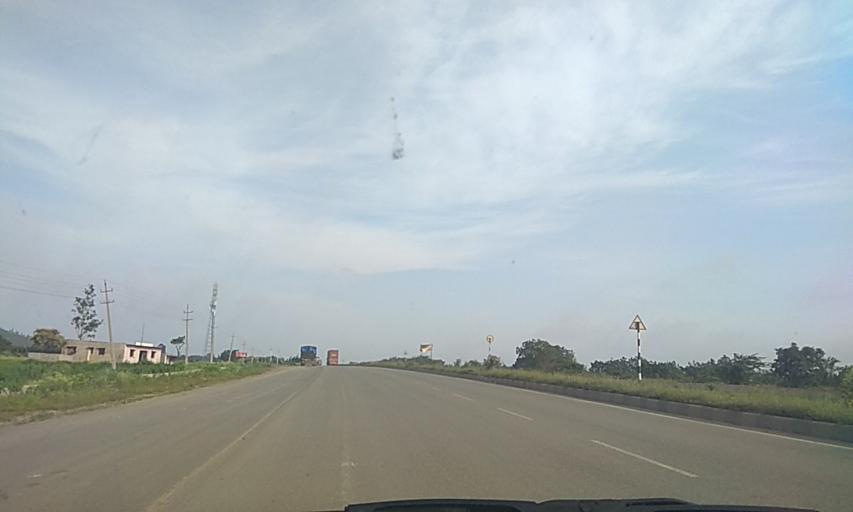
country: IN
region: Karnataka
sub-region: Haveri
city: Byadgi
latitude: 14.7013
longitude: 75.5224
